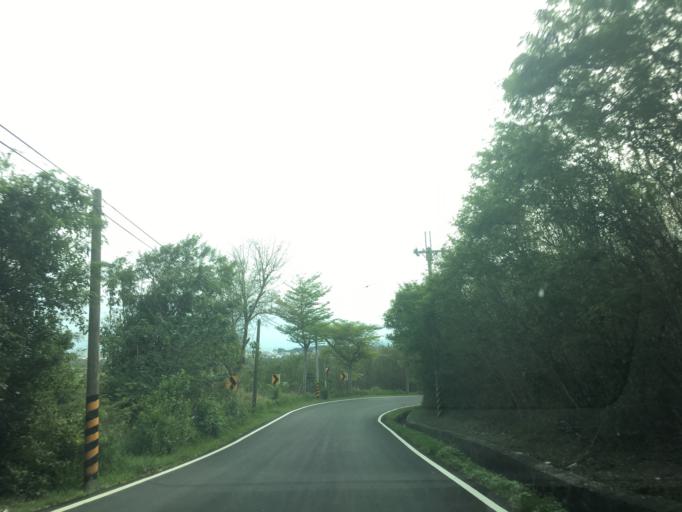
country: TW
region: Taiwan
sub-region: Taitung
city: Taitung
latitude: 22.7892
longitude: 121.1609
